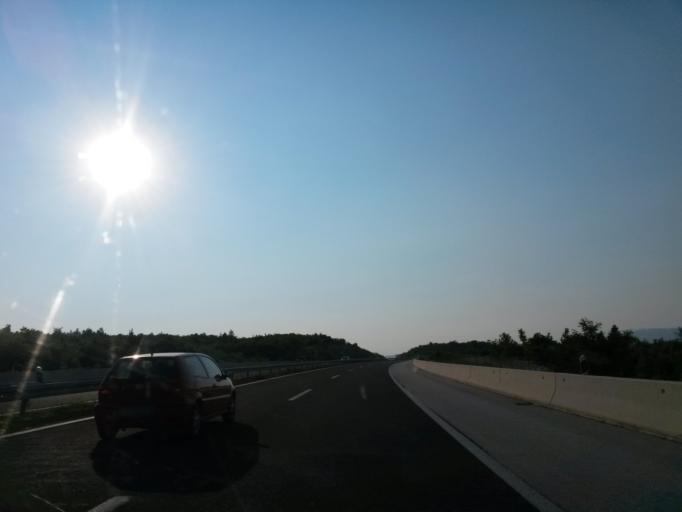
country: HR
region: Splitsko-Dalmatinska
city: Dugopolje
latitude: 43.5837
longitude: 16.6442
